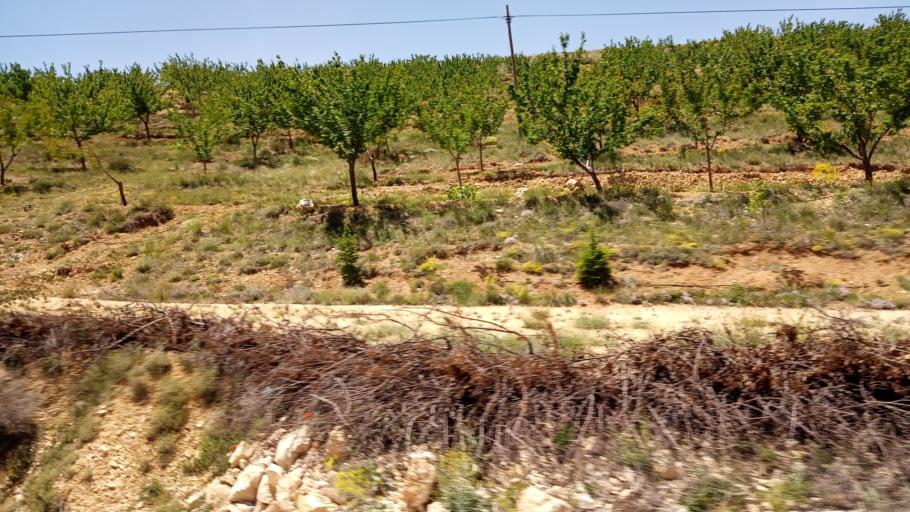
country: TR
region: Malatya
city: Darende
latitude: 38.6339
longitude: 37.4524
